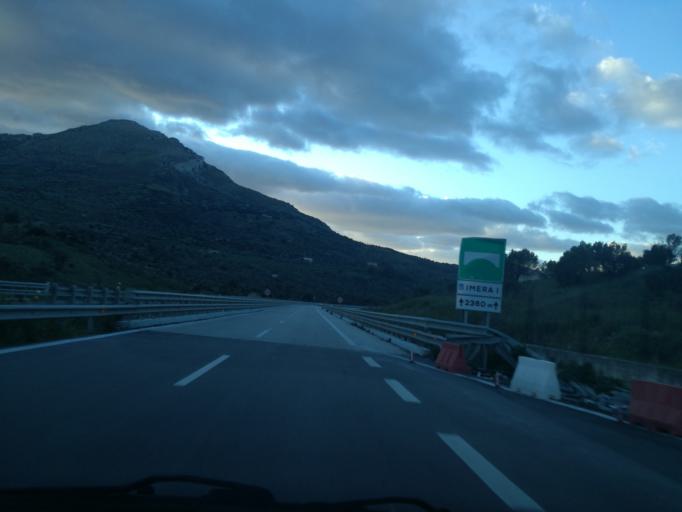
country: IT
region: Sicily
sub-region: Palermo
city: Scillato
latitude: 37.8359
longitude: 13.9331
